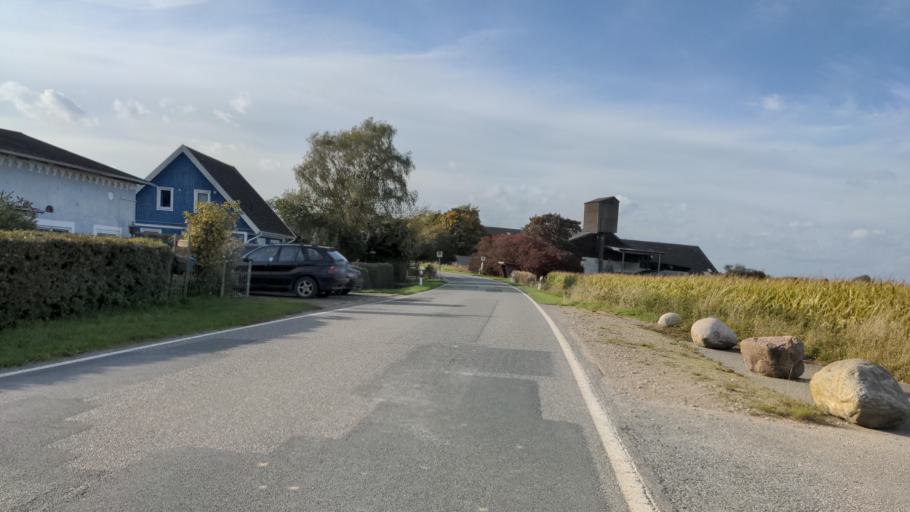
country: DE
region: Schleswig-Holstein
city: Monkhagen
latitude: 53.9544
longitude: 10.5383
